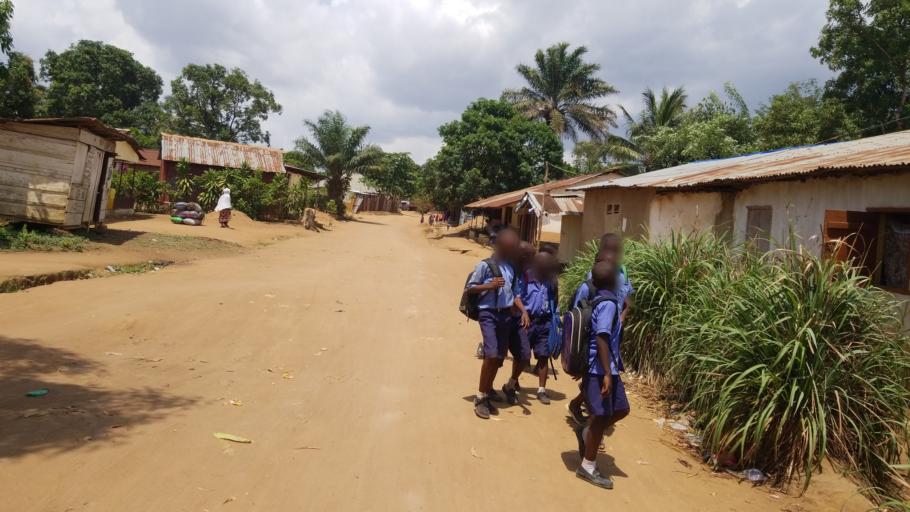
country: SL
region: Western Area
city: Waterloo
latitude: 8.3299
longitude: -13.0602
